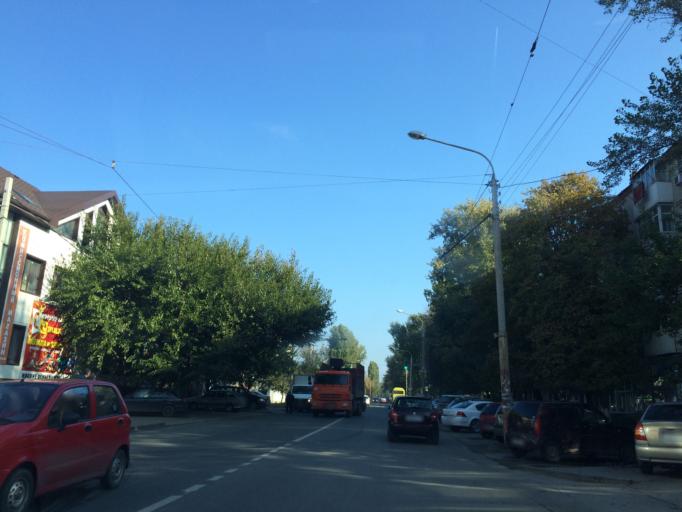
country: RU
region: Rostov
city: Imeni Chkalova
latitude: 47.2682
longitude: 39.7879
